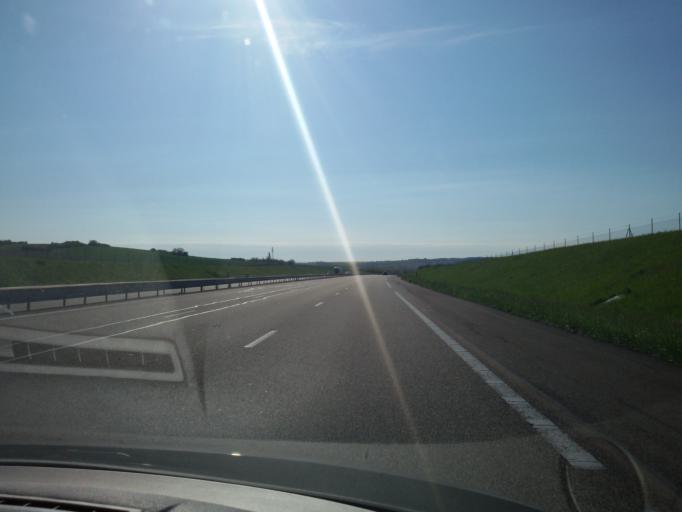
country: FR
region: Bourgogne
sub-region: Departement de l'Yonne
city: Aillant-sur-Tholon
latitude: 47.8944
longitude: 3.4007
